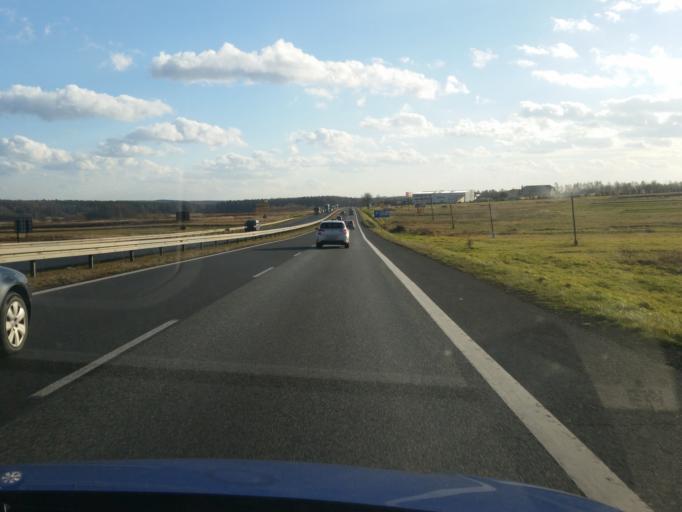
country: PL
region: Silesian Voivodeship
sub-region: Powiat myszkowski
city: Kozieglowy
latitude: 50.5598
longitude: 19.1757
